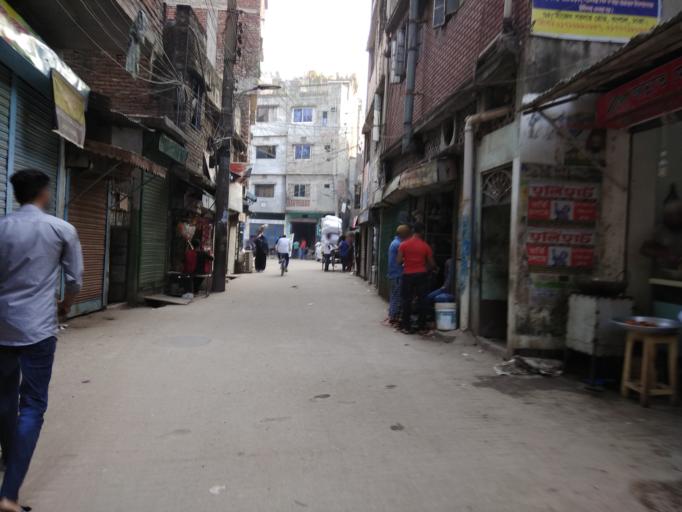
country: BD
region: Dhaka
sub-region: Dhaka
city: Dhaka
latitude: 23.7217
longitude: 90.4006
